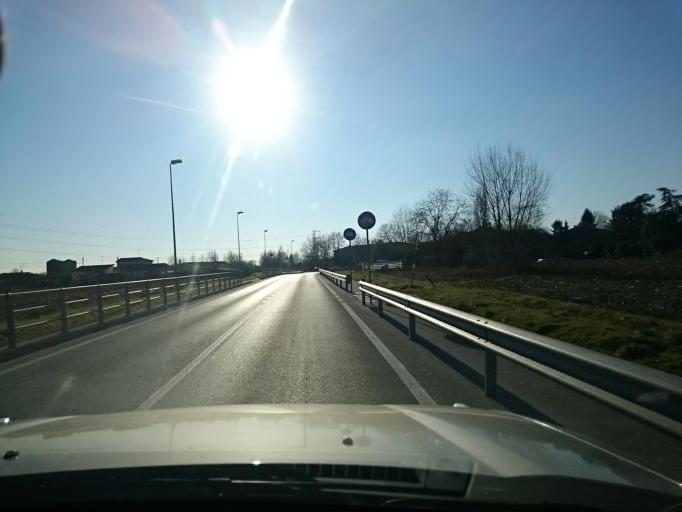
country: IT
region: Veneto
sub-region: Provincia di Venezia
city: Mira Taglio
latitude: 45.4353
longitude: 12.1510
